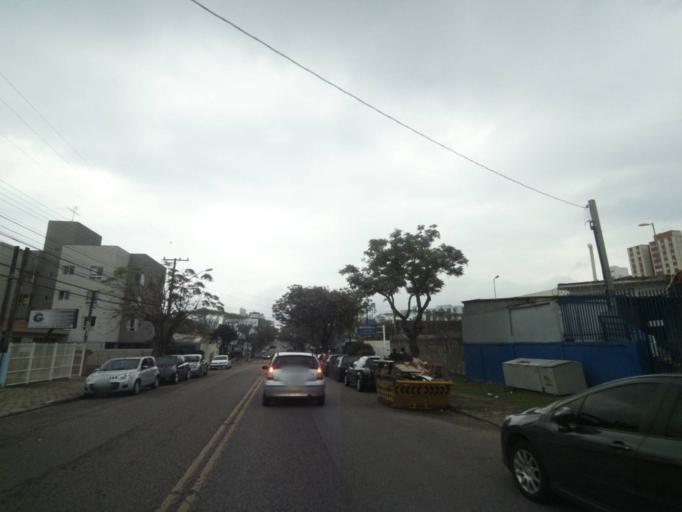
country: BR
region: Parana
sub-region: Curitiba
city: Curitiba
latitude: -25.4787
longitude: -49.2969
